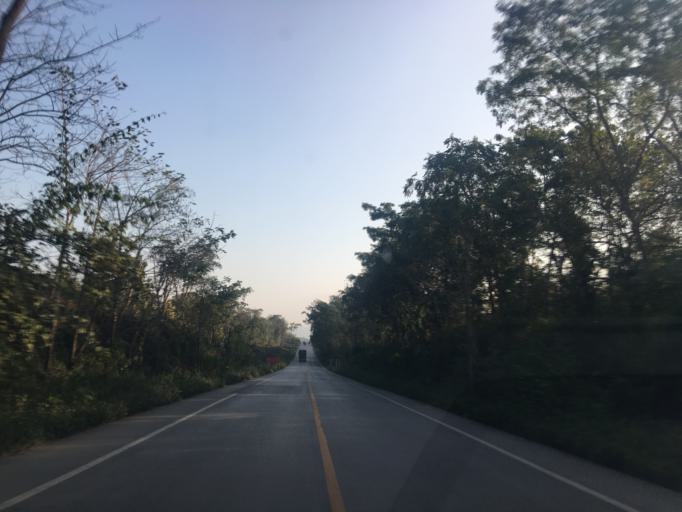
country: TH
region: Lampang
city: Ngao
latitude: 18.6553
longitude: 100.0176
